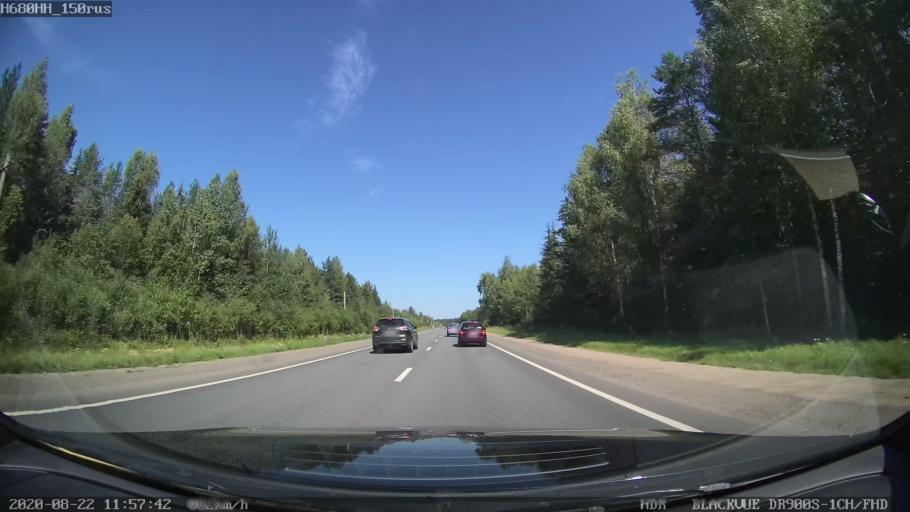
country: RU
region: Tverskaya
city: Rameshki
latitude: 57.1834
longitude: 36.0818
